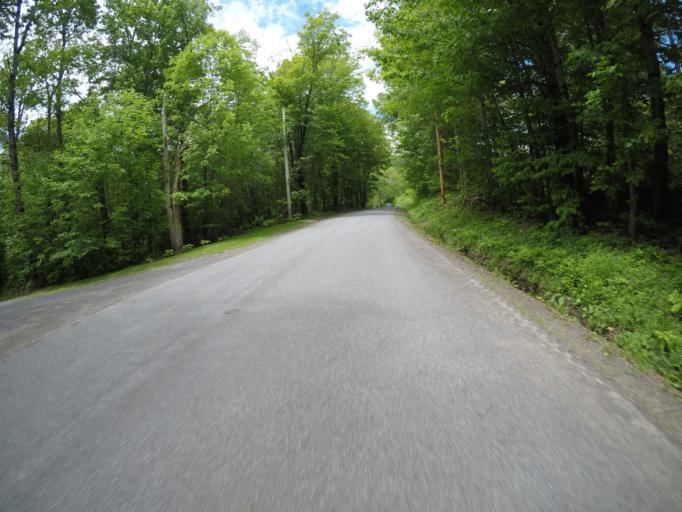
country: US
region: New York
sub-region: Delaware County
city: Stamford
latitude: 42.2803
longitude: -74.5124
